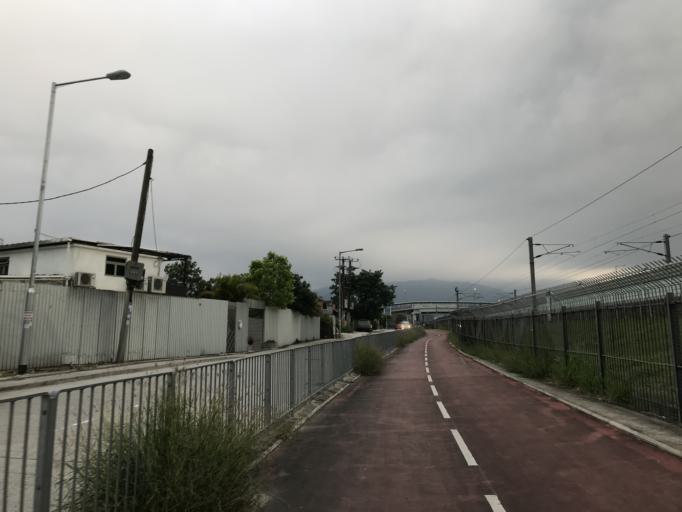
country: HK
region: Tai Po
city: Tai Po
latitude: 22.4777
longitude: 114.1550
